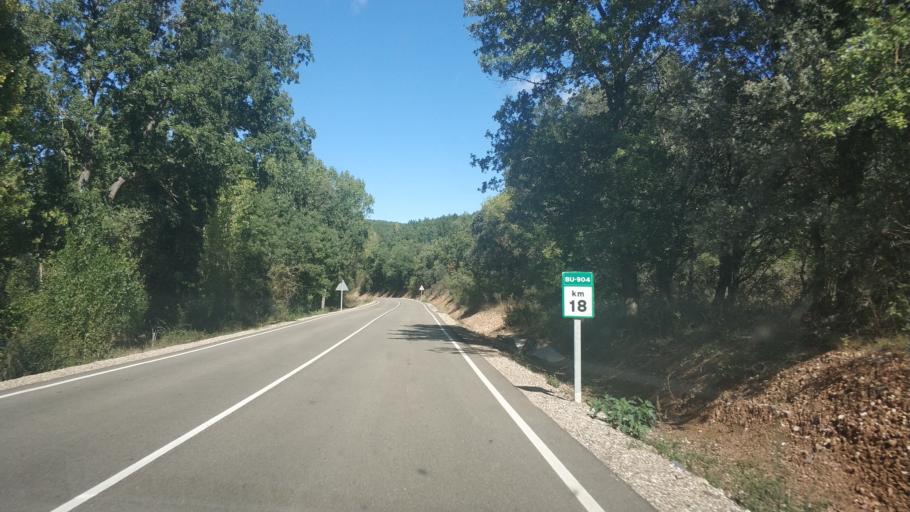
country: ES
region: Castille and Leon
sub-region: Provincia de Burgos
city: Covarrubias
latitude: 42.0486
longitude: -3.5500
